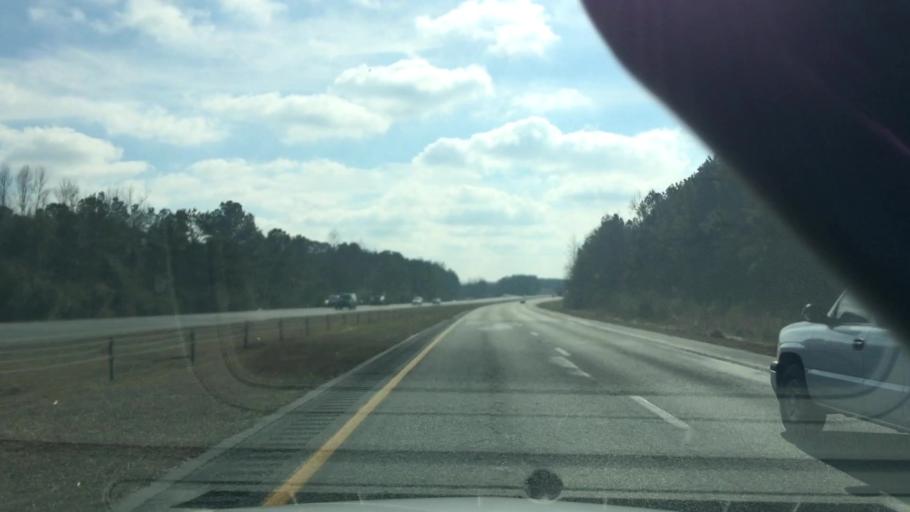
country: US
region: North Carolina
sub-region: Duplin County
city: Wallace
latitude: 34.6956
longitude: -77.9448
